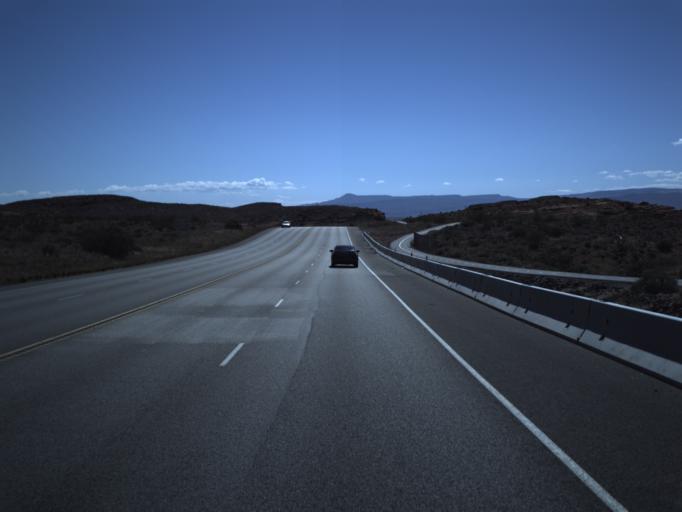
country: US
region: Utah
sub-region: Washington County
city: Saint George
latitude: 37.1433
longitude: -113.6056
